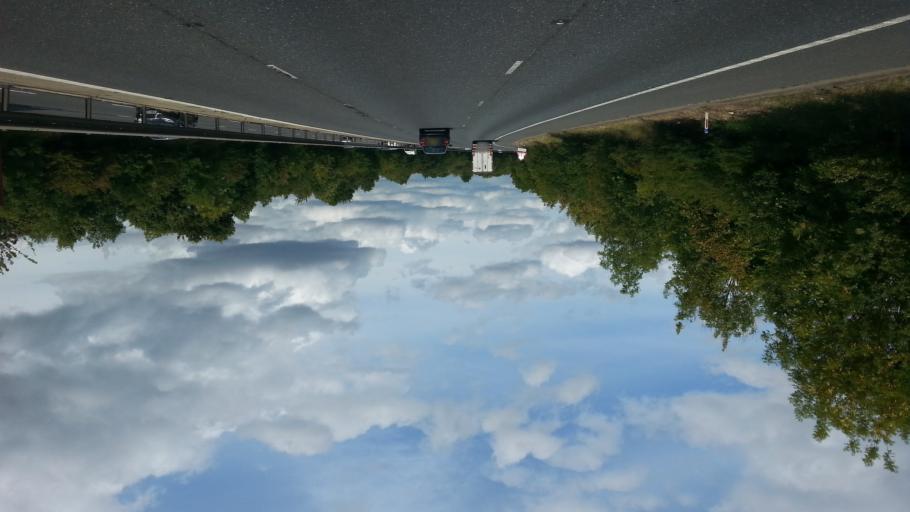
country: GB
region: England
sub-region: Essex
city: Little Hallingbury
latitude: 51.8301
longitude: 0.1911
